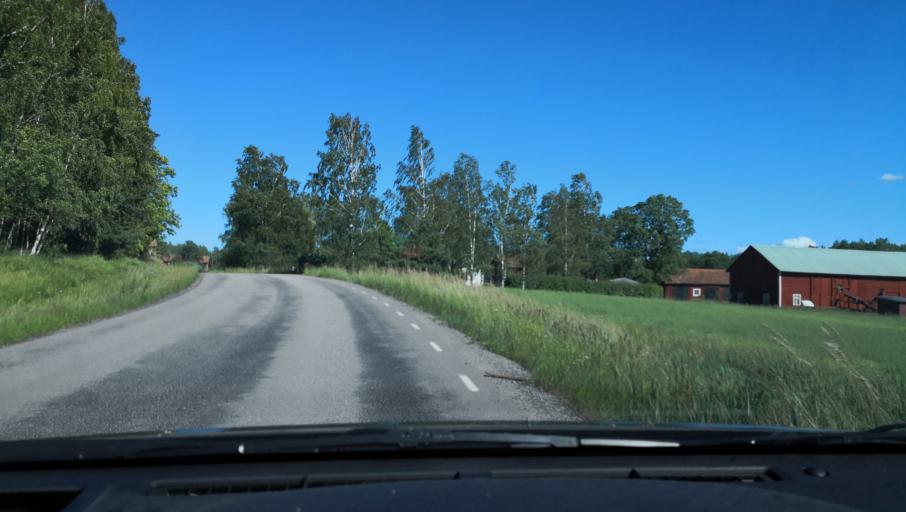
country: SE
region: Soedermanland
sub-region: Eskilstuna Kommun
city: Arla
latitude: 59.3233
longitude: 16.6164
